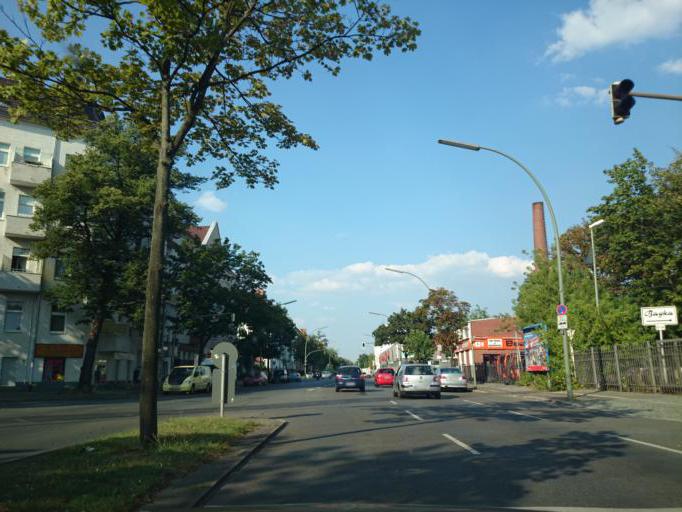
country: DE
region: Berlin
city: Tegel
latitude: 52.5802
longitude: 13.3020
